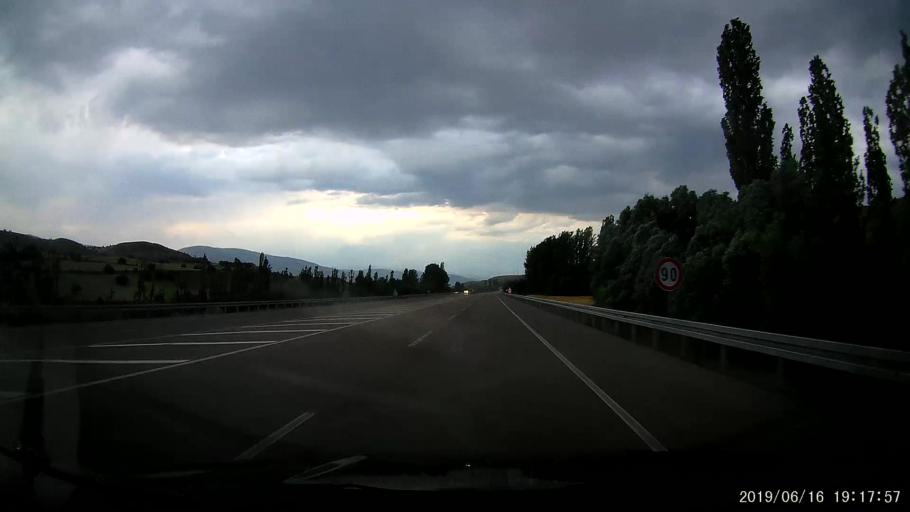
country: TR
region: Sivas
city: Akincilar
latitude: 40.0942
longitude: 38.4713
